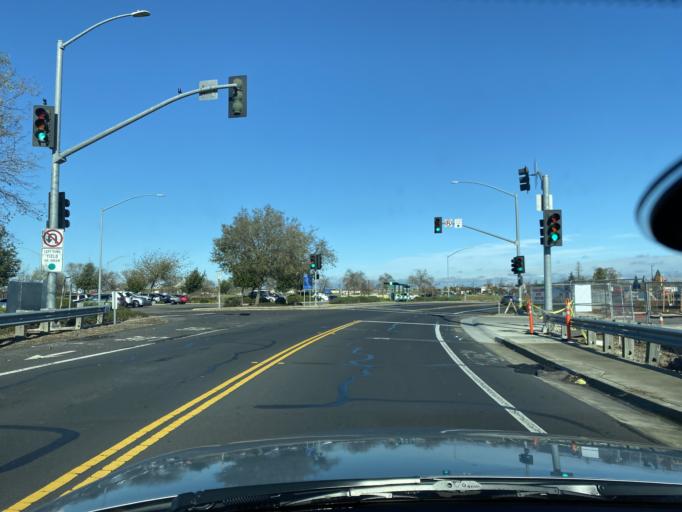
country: US
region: California
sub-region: Sacramento County
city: Laguna
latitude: 38.4348
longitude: -121.3995
